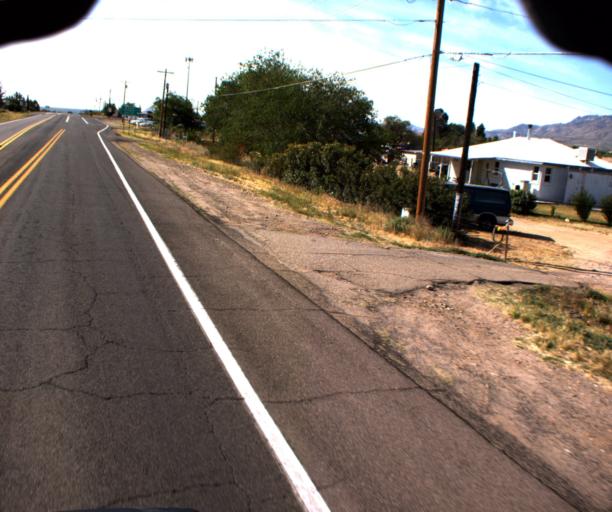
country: US
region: Arizona
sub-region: Graham County
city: Swift Trail Junction
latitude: 32.7316
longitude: -109.7151
